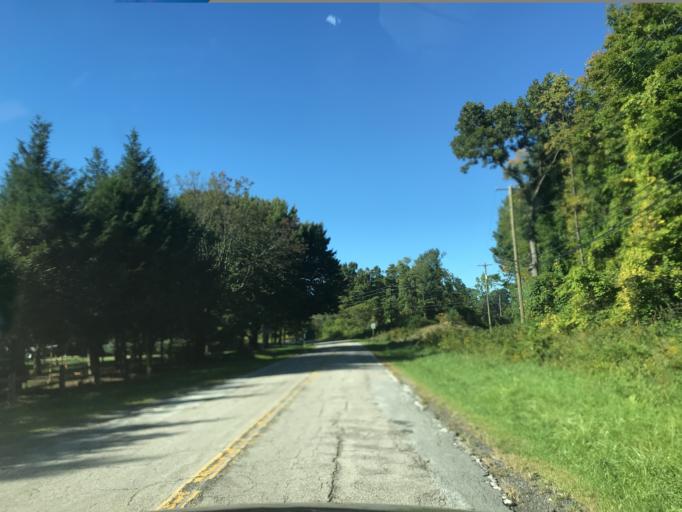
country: US
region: Ohio
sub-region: Lake County
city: Perry
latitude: 41.7206
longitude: -81.1807
